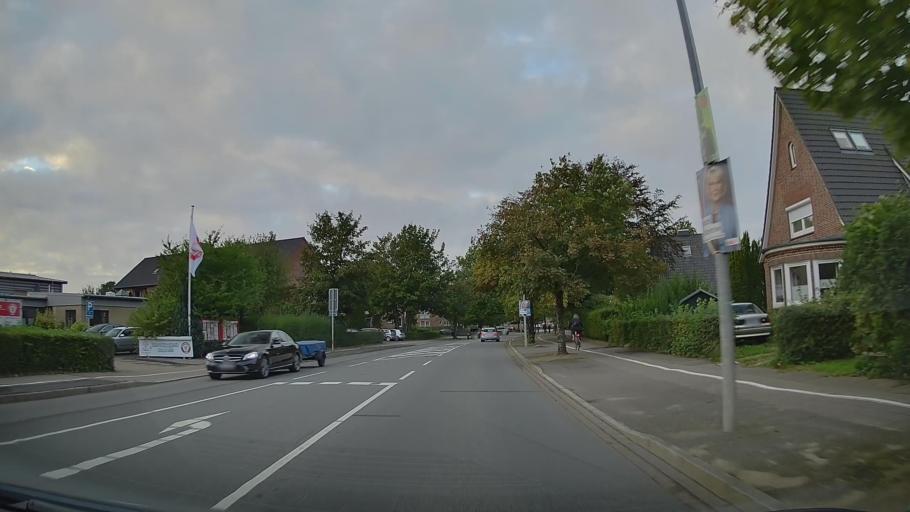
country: DE
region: Schleswig-Holstein
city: Husum
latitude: 54.4837
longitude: 9.0542
